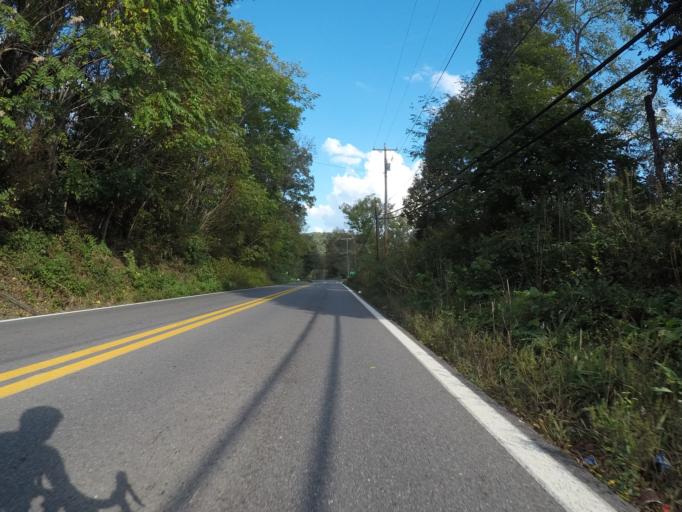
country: US
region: Ohio
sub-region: Lawrence County
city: Burlington
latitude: 38.3845
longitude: -82.5145
